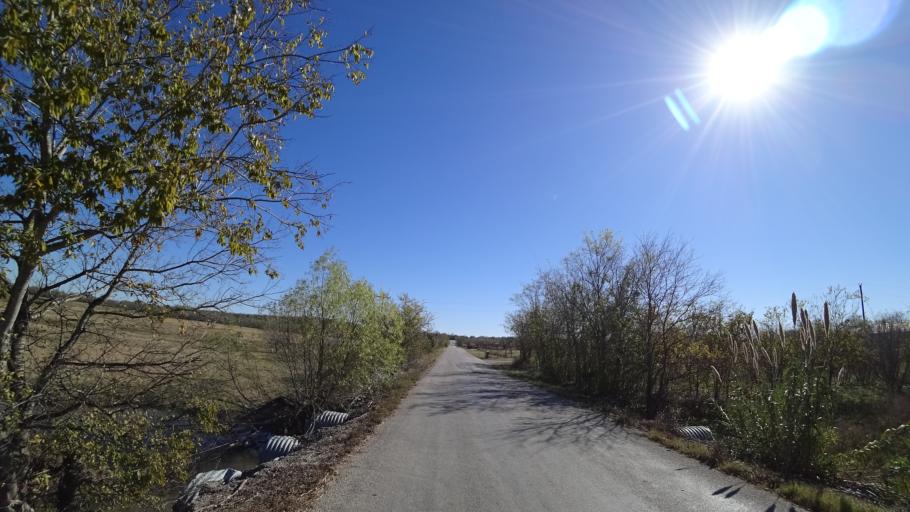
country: US
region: Texas
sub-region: Travis County
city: Garfield
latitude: 30.1164
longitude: -97.5902
